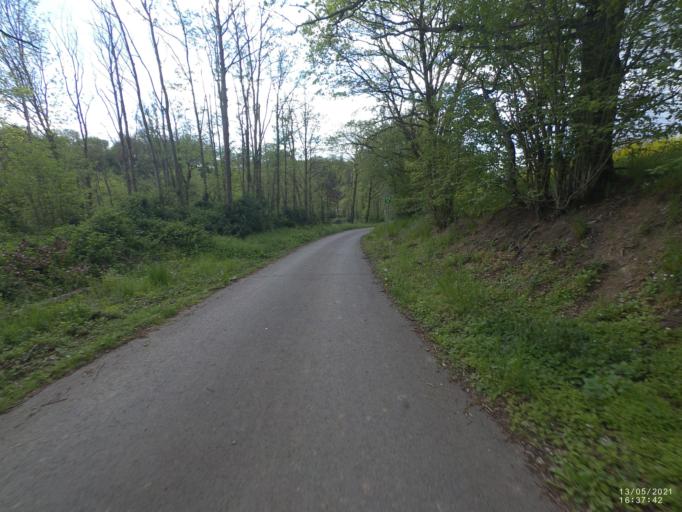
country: DE
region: Rheinland-Pfalz
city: Dieblich
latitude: 50.3232
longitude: 7.4595
